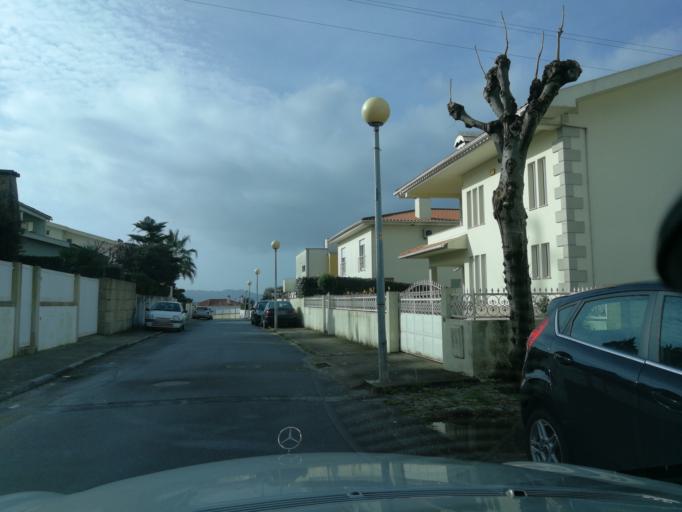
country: PT
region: Braga
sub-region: Braga
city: Braga
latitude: 41.5346
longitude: -8.4137
